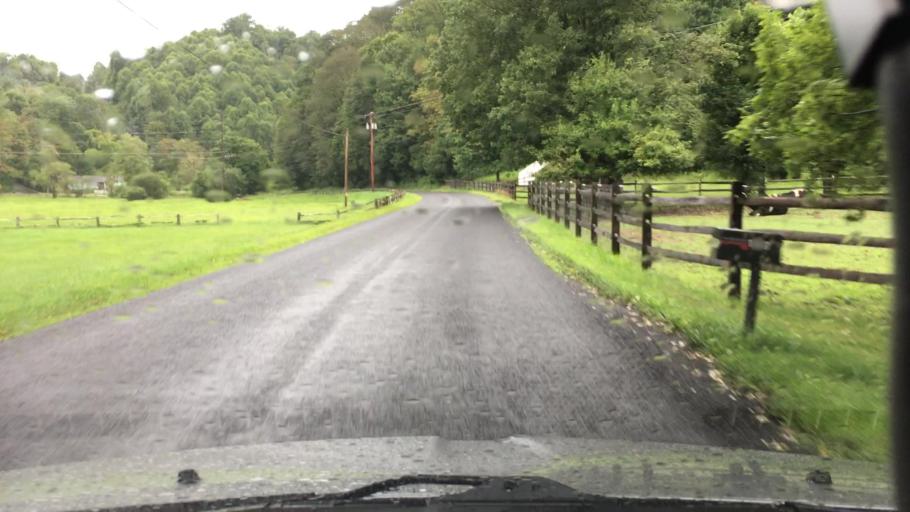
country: US
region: North Carolina
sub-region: Madison County
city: Mars Hill
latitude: 35.9105
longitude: -82.5254
